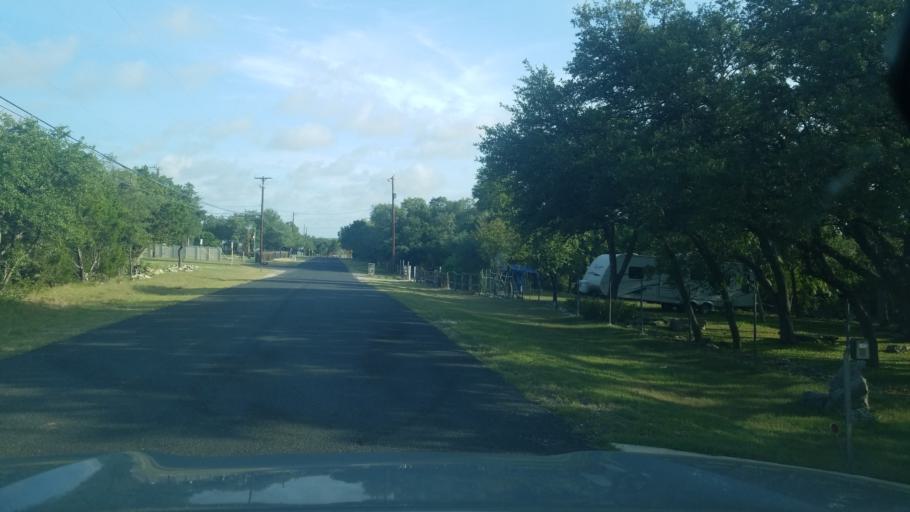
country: US
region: Texas
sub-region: Bexar County
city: Timberwood Park
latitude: 29.7048
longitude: -98.5172
